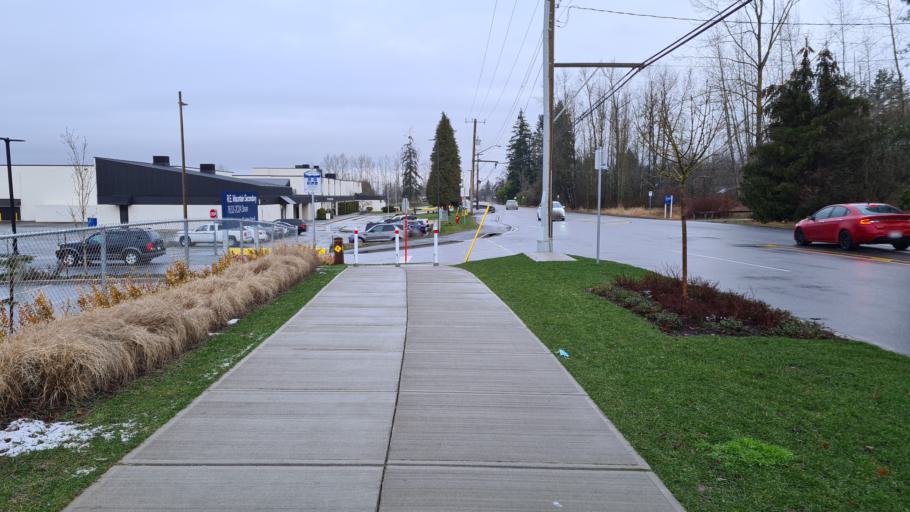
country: CA
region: British Columbia
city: Walnut Grove
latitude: 49.1427
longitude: -122.6617
